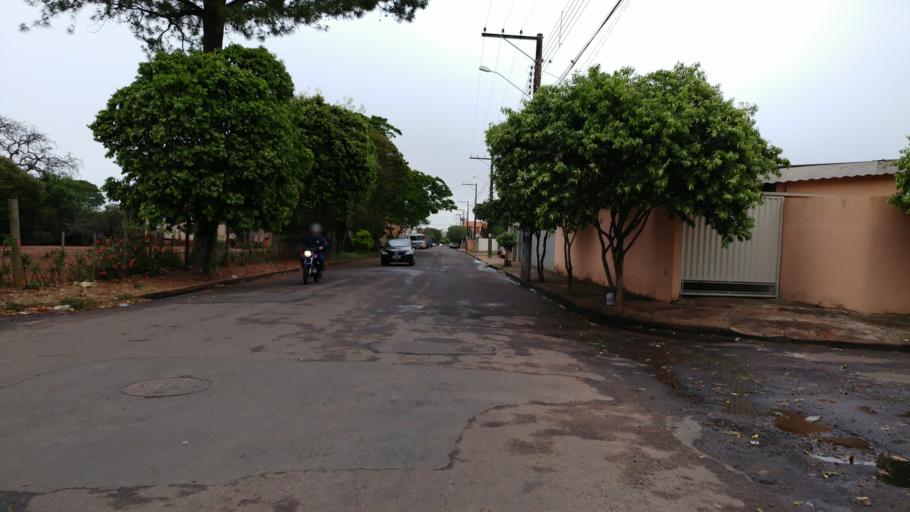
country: BR
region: Sao Paulo
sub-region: Paraguacu Paulista
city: Paraguacu Paulista
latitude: -22.4198
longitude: -50.5832
